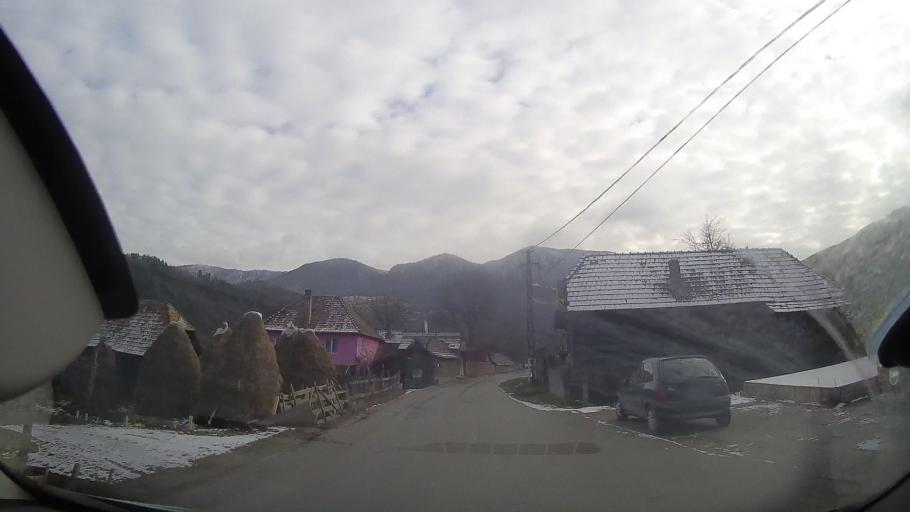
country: RO
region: Alba
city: Salciua de Sus
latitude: 46.4292
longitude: 23.4413
